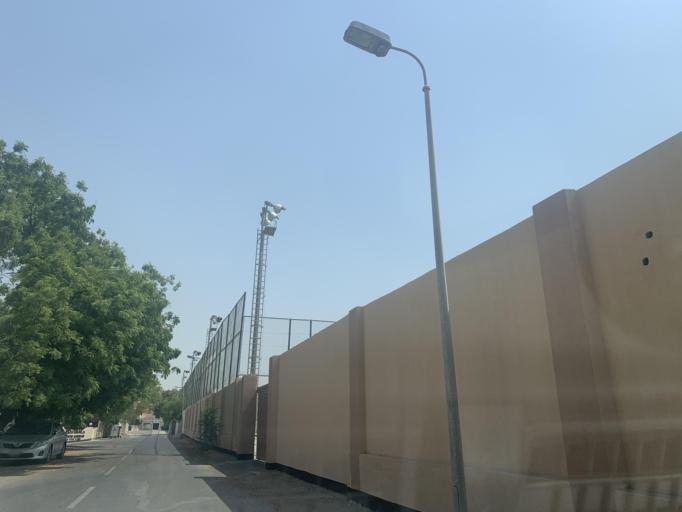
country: BH
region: Manama
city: Jidd Hafs
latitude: 26.2002
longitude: 50.4879
